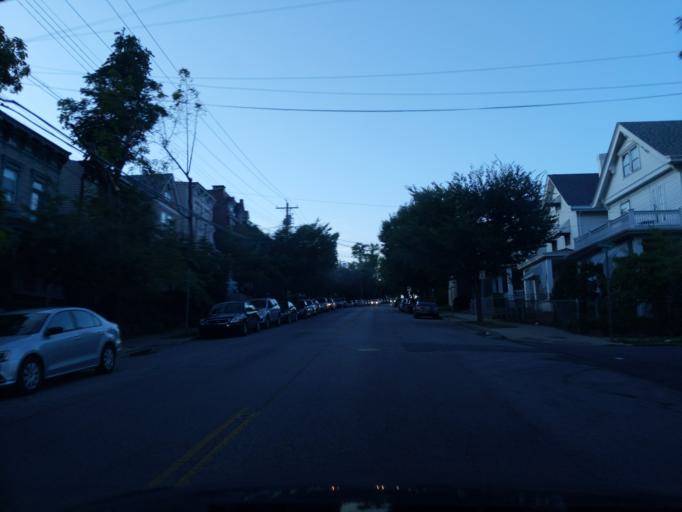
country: US
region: Kentucky
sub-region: Campbell County
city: Newport
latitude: 39.1253
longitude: -84.5197
